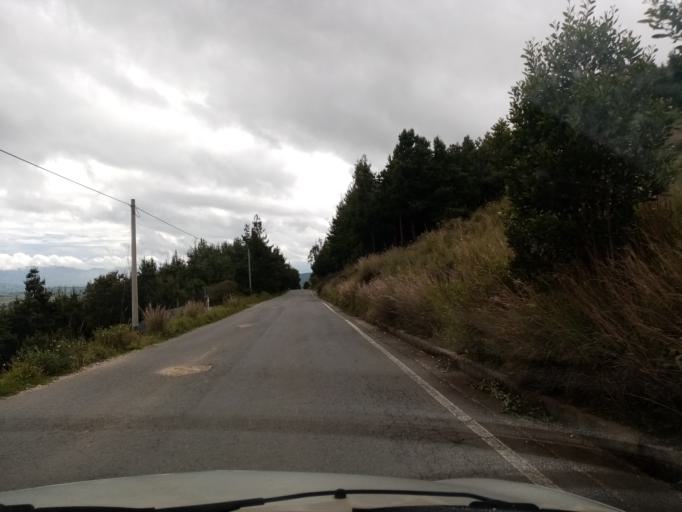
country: CO
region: Boyaca
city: Siachoque
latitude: 5.5729
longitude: -73.2728
